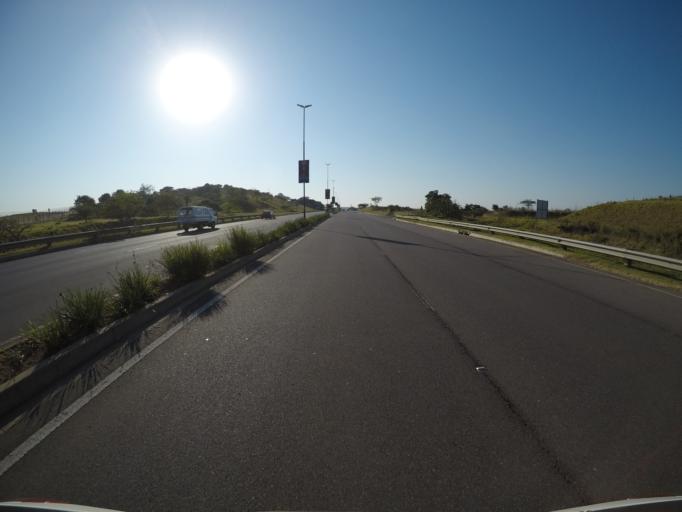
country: ZA
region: KwaZulu-Natal
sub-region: iLembe District Municipality
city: Ballitoville
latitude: -29.6283
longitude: 31.1088
